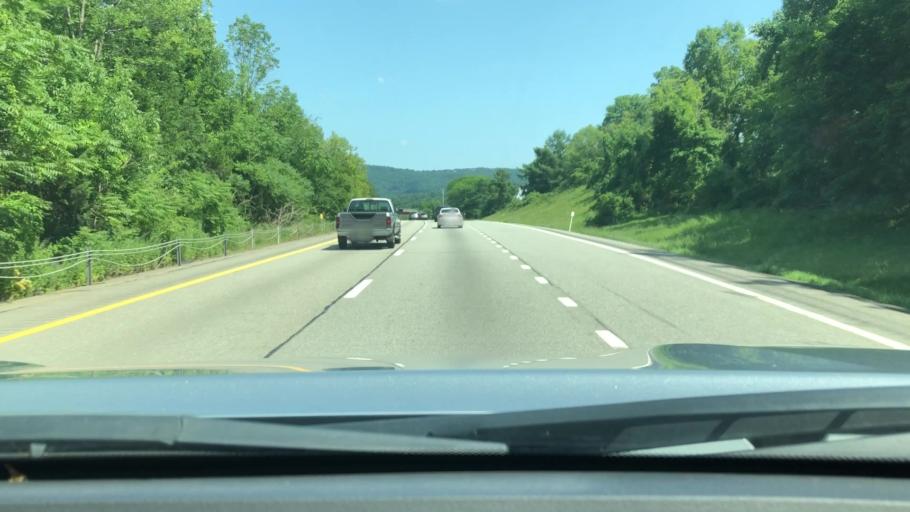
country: US
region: New York
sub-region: Dutchess County
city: Brinckerhoff
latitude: 41.5302
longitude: -73.8168
